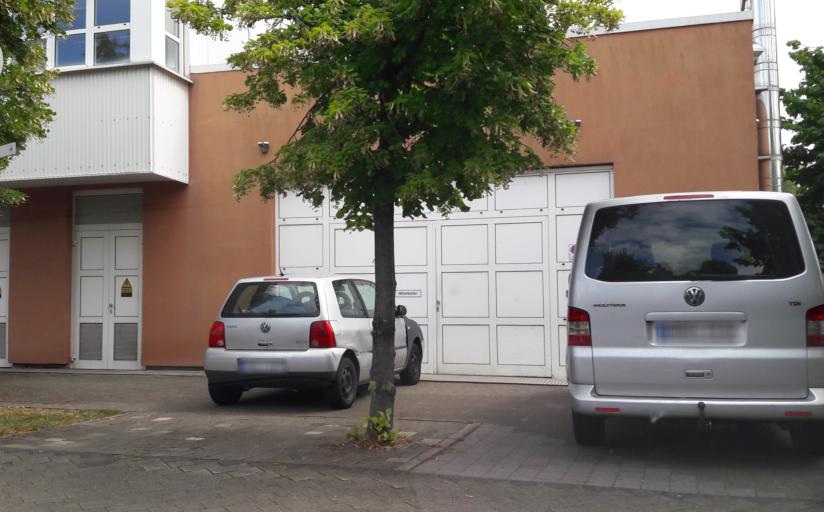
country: DE
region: Saarland
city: Tholey
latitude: 49.4911
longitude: 7.0383
